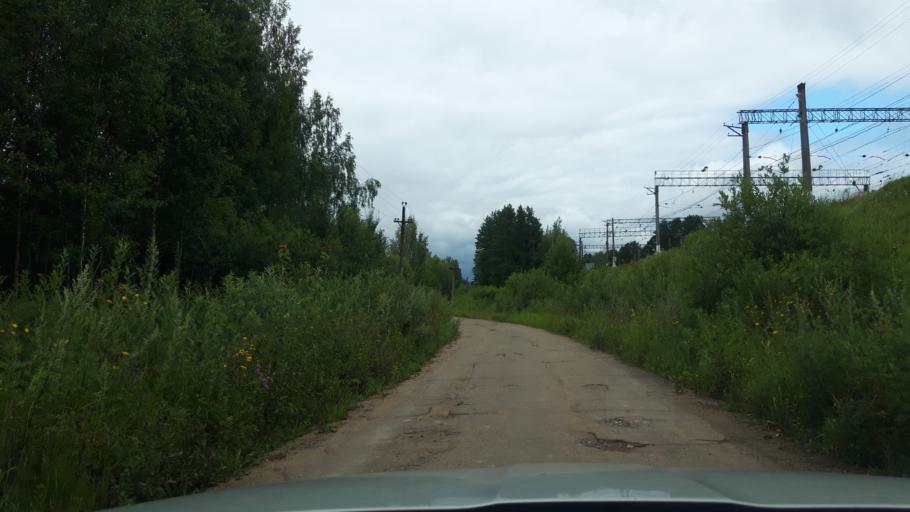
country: RU
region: Moskovskaya
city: Povarovo
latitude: 56.0536
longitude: 37.0577
